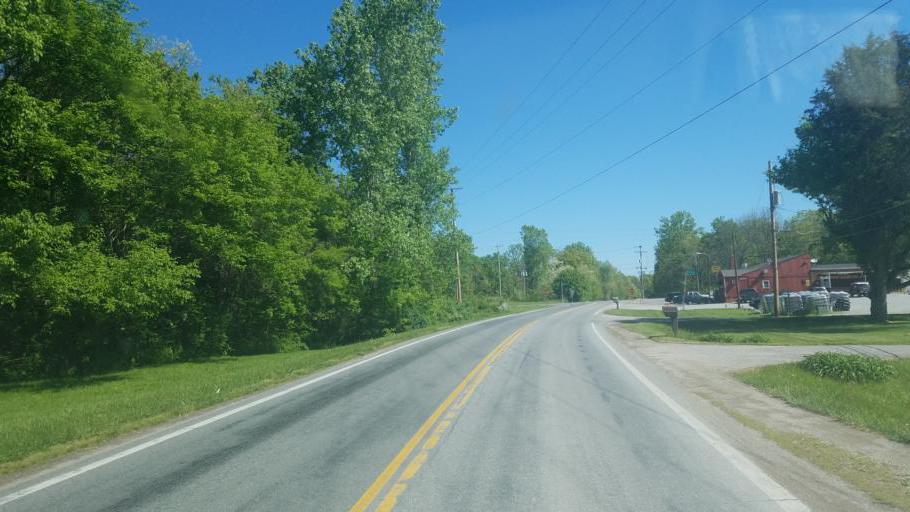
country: US
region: Ohio
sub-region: Delaware County
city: Lewis Center
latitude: 40.2375
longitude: -82.9627
